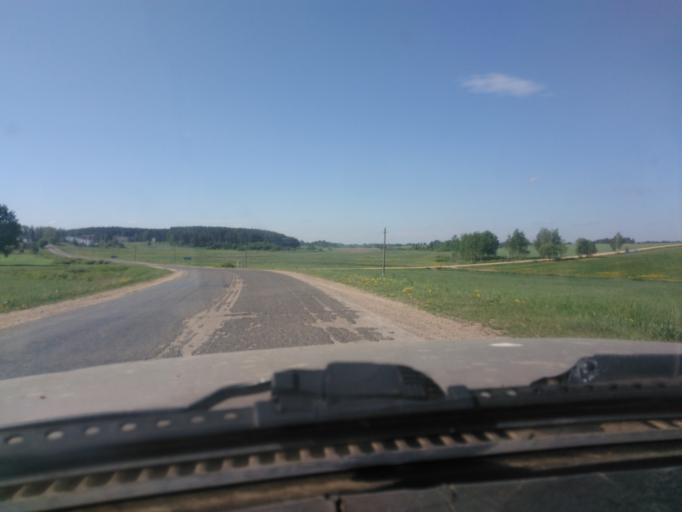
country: BY
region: Mogilev
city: Myazhysyatki
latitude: 53.7880
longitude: 30.0098
